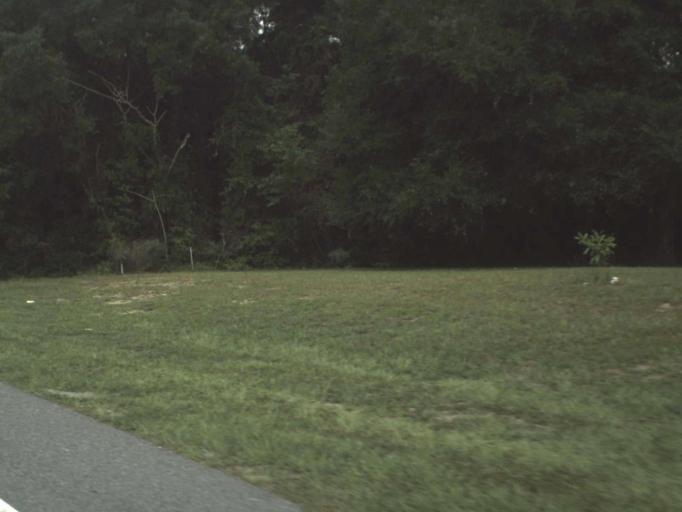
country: US
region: Florida
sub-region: Sumter County
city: Lake Panasoffkee
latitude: 28.7300
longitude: -82.0729
